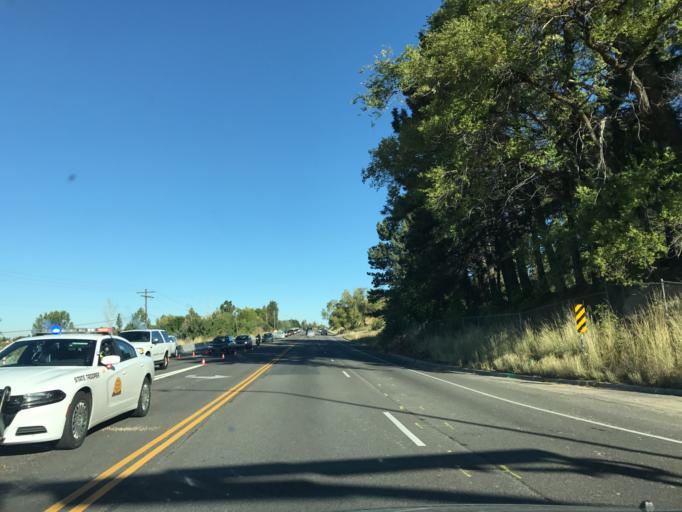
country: US
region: Utah
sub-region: Weber County
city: Washington Terrace
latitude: 41.1683
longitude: -111.9451
